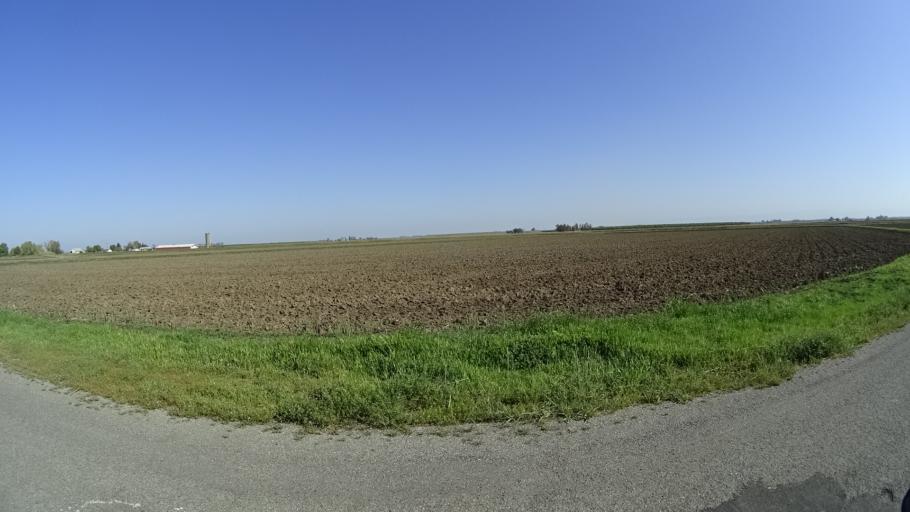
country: US
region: California
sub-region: Glenn County
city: Hamilton City
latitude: 39.6016
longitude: -122.0504
